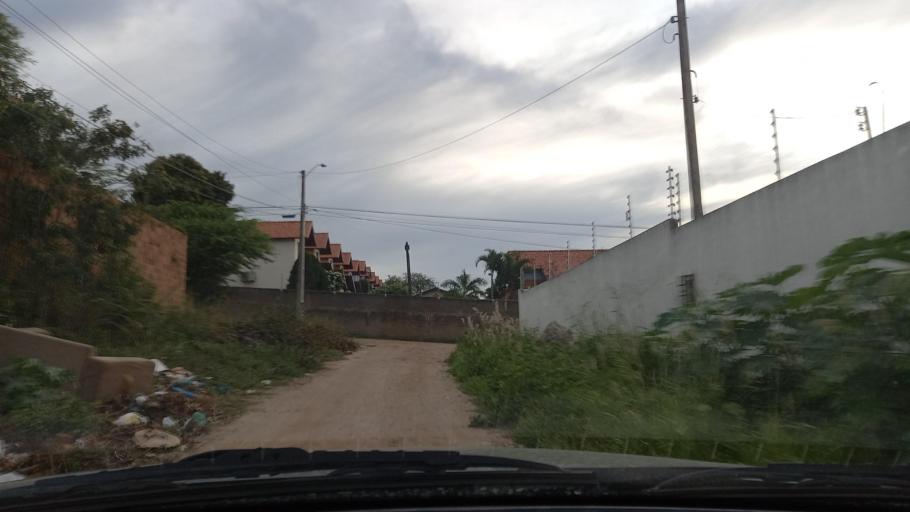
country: BR
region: Pernambuco
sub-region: Gravata
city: Gravata
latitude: -8.1955
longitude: -35.5811
